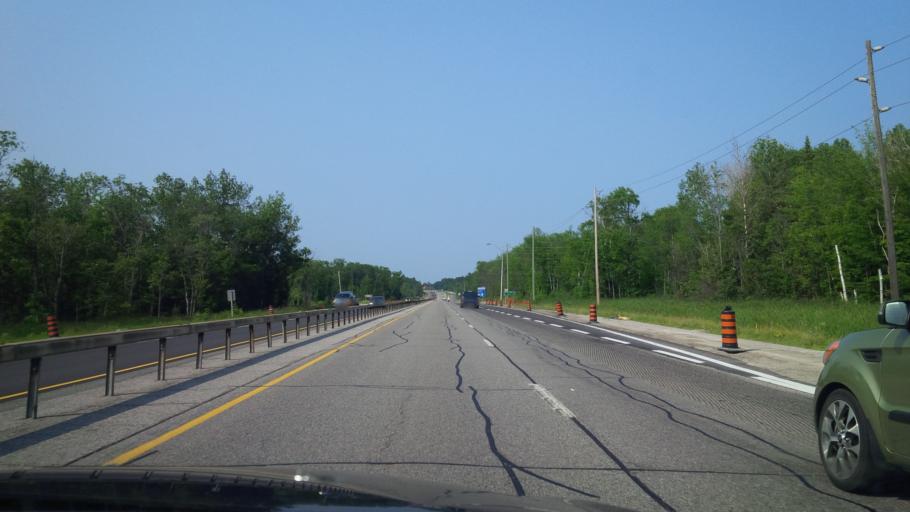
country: CA
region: Ontario
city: Orillia
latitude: 44.7347
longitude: -79.3596
